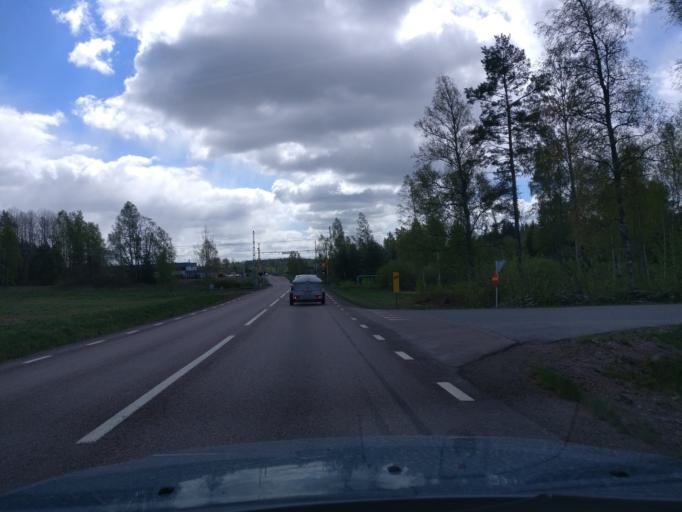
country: SE
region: Vaermland
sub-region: Karlstads Kommun
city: Molkom
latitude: 59.6105
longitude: 13.7359
